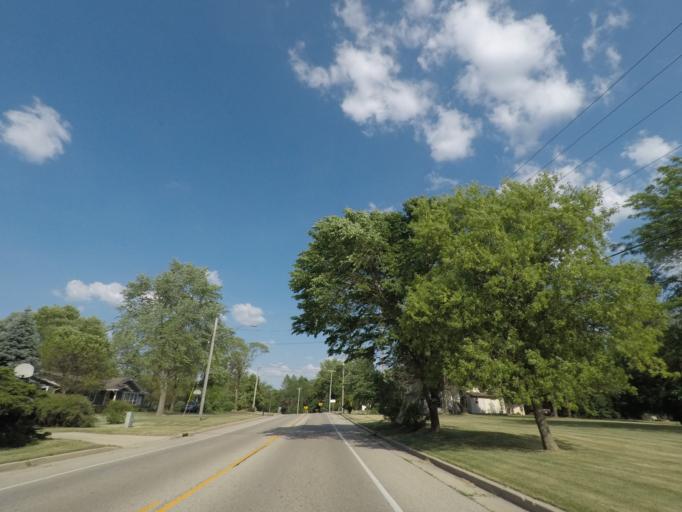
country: US
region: Wisconsin
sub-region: Walworth County
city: East Troy
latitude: 42.7912
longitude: -88.4157
